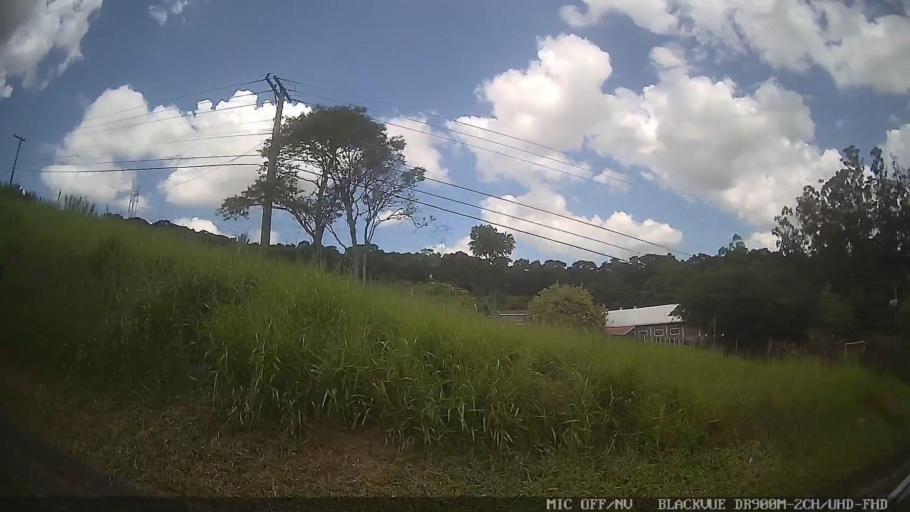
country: BR
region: Sao Paulo
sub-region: Sao Jose Dos Campos
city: Sao Jose dos Campos
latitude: -23.2695
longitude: -45.8176
